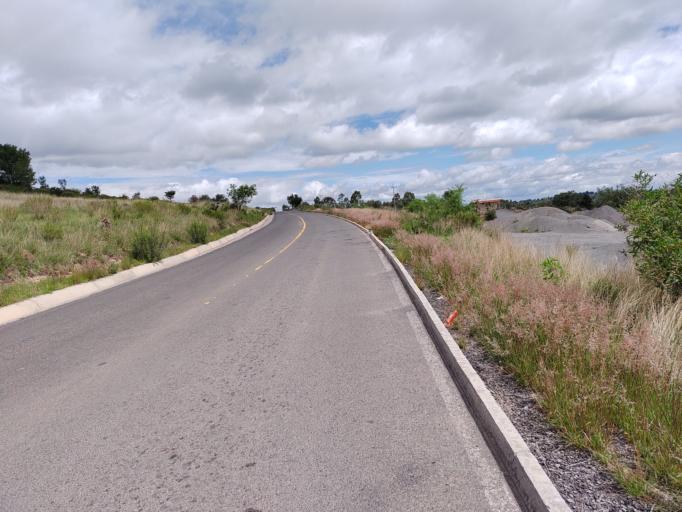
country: MX
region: Mexico
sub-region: Aculco
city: Gunyo Poniente (San Jose Gunyo)
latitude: 20.1117
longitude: -99.8667
